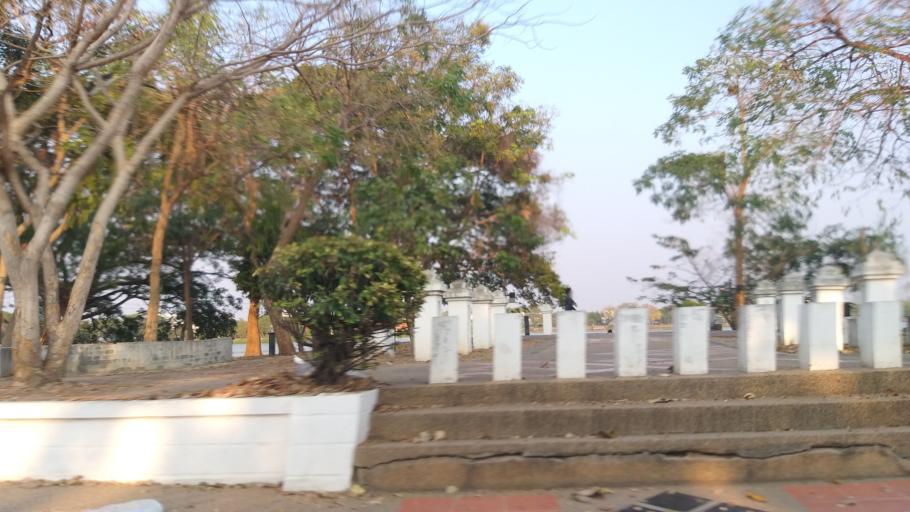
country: TH
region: Khon Kaen
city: Khon Kaen
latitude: 16.4161
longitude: 102.8350
